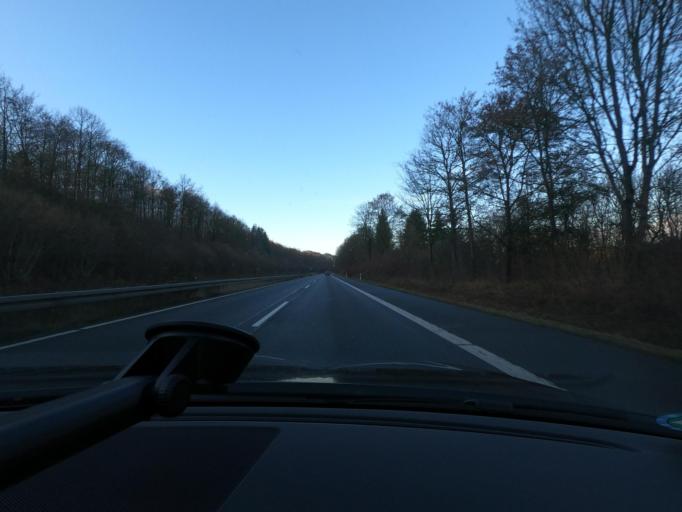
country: DE
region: Lower Saxony
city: Hoerden
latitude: 51.7038
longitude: 10.2808
